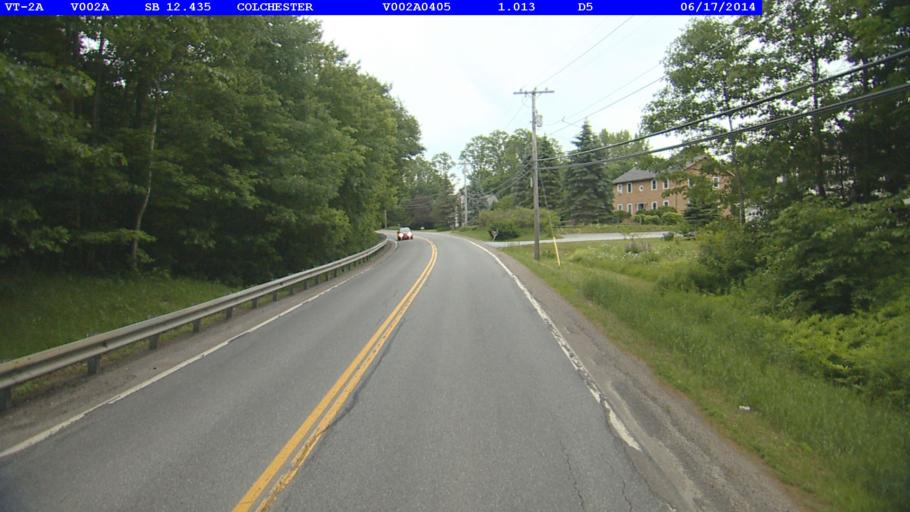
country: US
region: Vermont
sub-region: Chittenden County
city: Colchester
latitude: 44.5392
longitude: -73.1417
